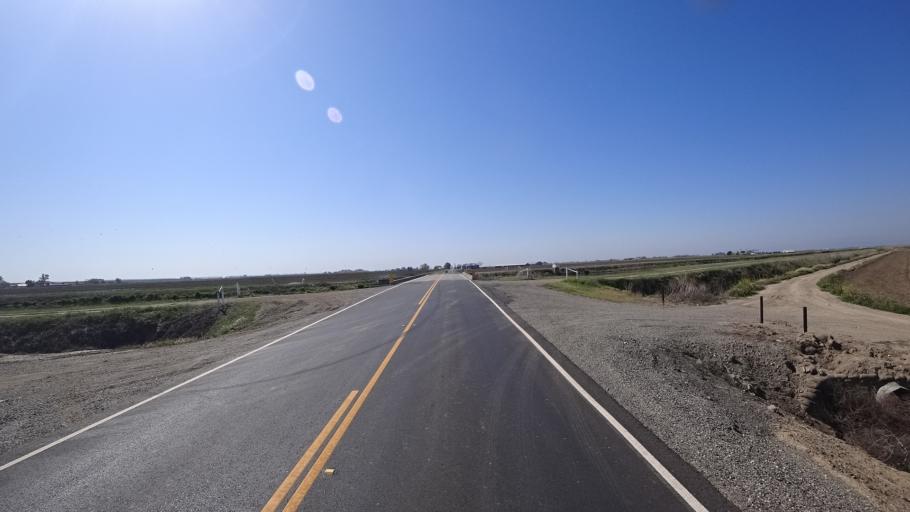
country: US
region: California
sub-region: Glenn County
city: Hamilton City
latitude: 39.6272
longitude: -122.0650
